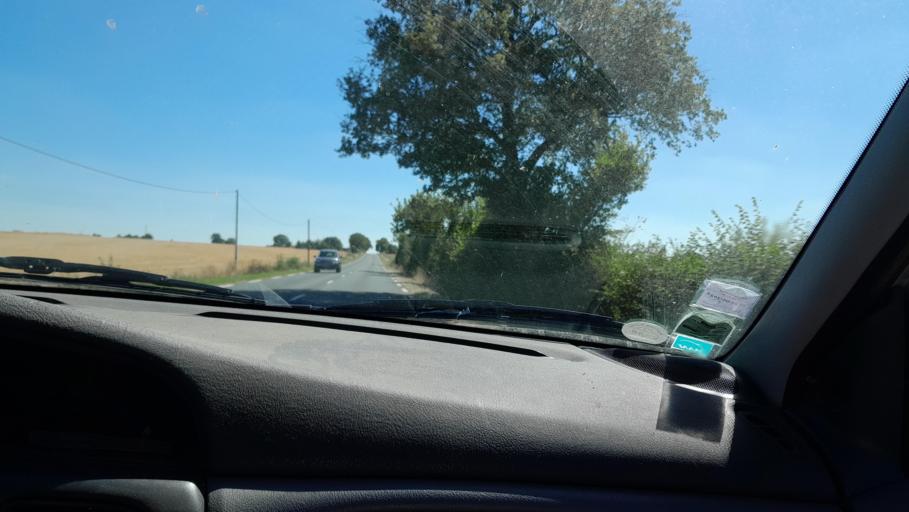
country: FR
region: Pays de la Loire
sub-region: Departement de la Loire-Atlantique
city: Saint-Mars-la-Jaille
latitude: 47.4785
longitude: -1.1743
